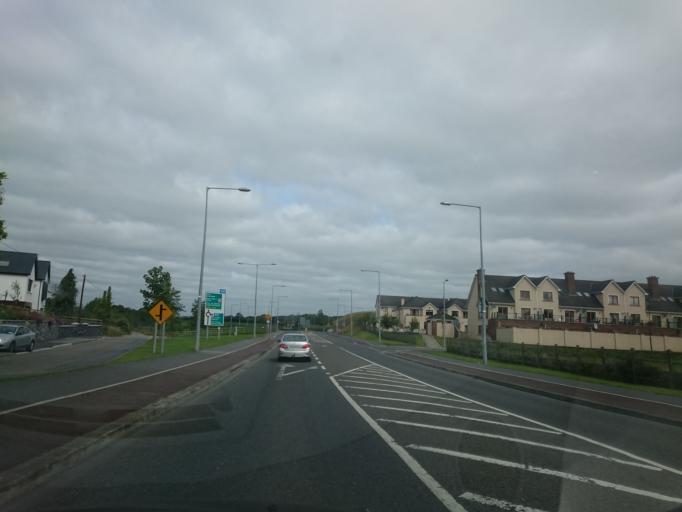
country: IE
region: Leinster
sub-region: Kilkenny
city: Kilkenny
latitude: 52.6749
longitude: -7.2537
